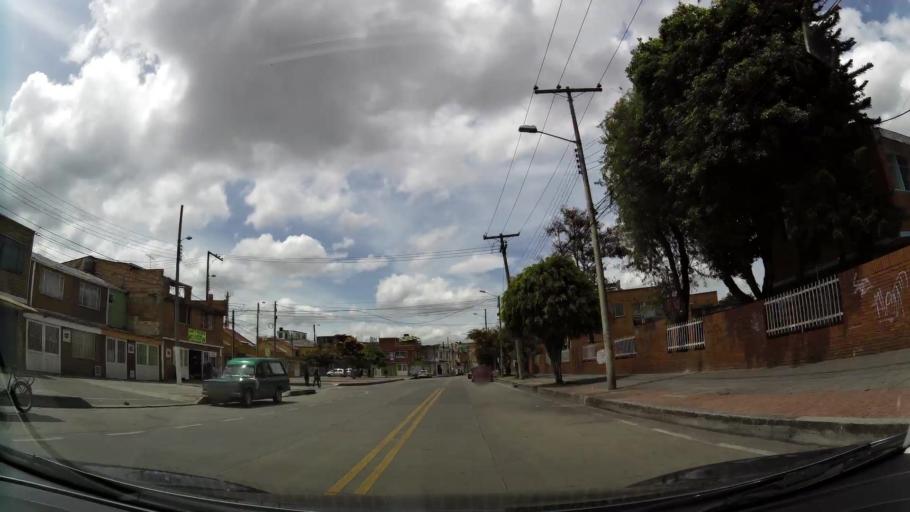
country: CO
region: Cundinamarca
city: Funza
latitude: 4.7070
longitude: -74.1171
